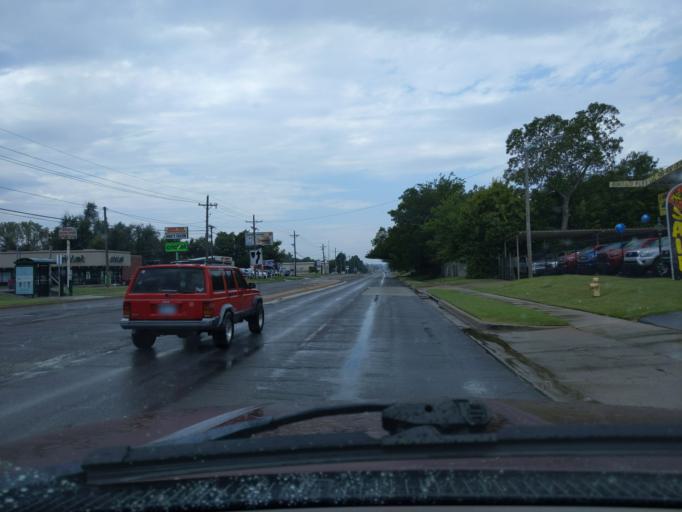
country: US
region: Oklahoma
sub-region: Tulsa County
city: Broken Arrow
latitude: 36.1335
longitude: -95.8348
